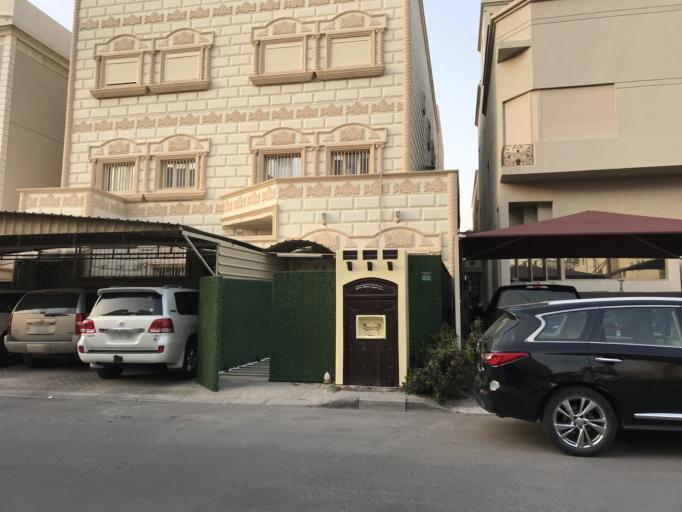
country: KW
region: Al Asimah
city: Ar Rabiyah
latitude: 29.2435
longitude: 47.9066
